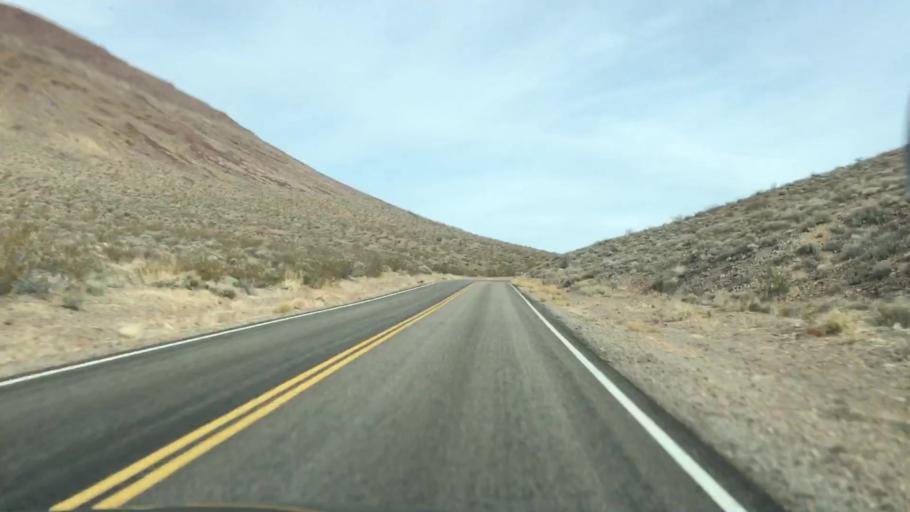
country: US
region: Nevada
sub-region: Nye County
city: Beatty
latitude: 36.7766
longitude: -116.9331
